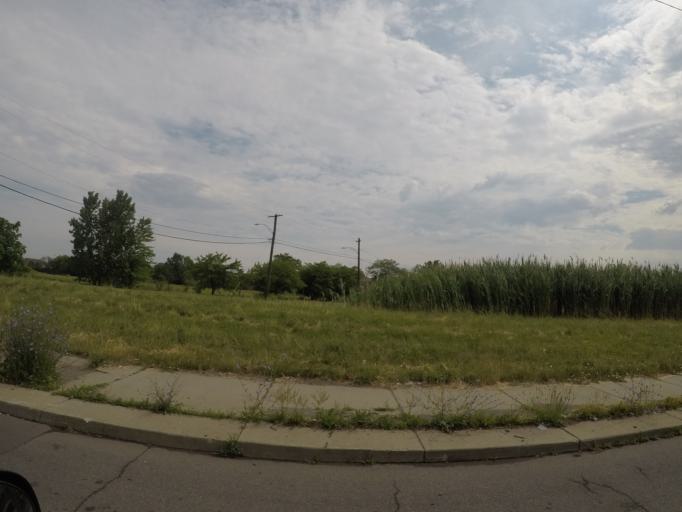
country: US
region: Michigan
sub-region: Wayne County
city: Detroit
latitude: 42.3459
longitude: -83.0822
